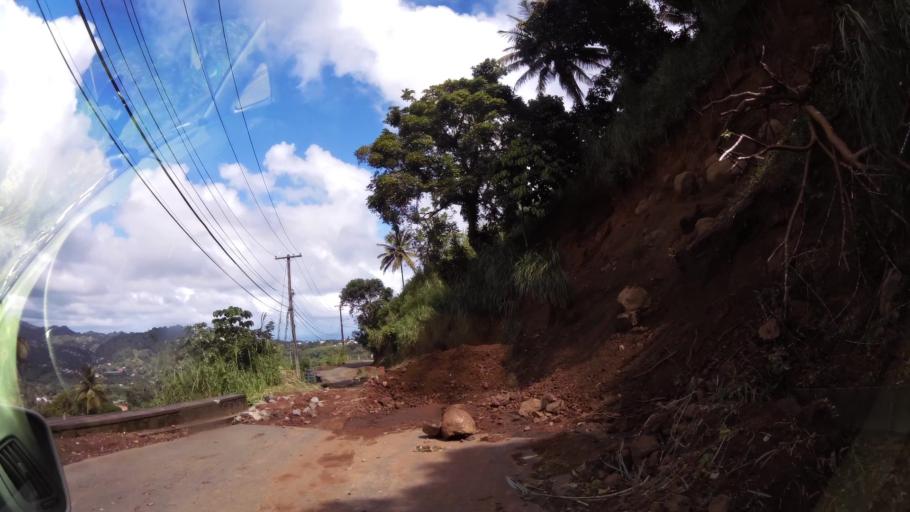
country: VC
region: Saint George
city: Kingstown
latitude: 13.1647
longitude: -61.1764
